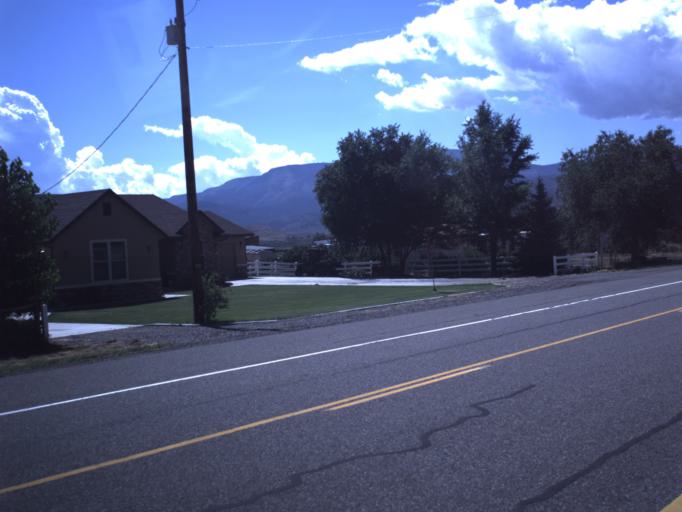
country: US
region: Utah
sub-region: Piute County
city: Junction
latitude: 38.2441
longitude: -112.2201
